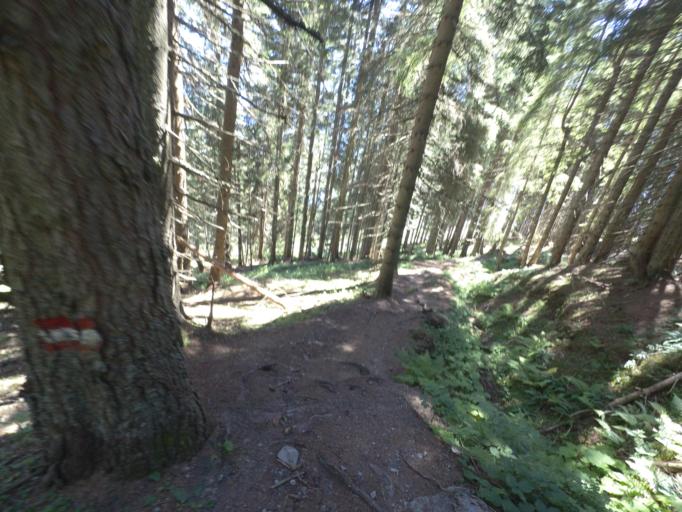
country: AT
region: Salzburg
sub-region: Politischer Bezirk Sankt Johann im Pongau
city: Goldegg
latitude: 47.3387
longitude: 13.0659
